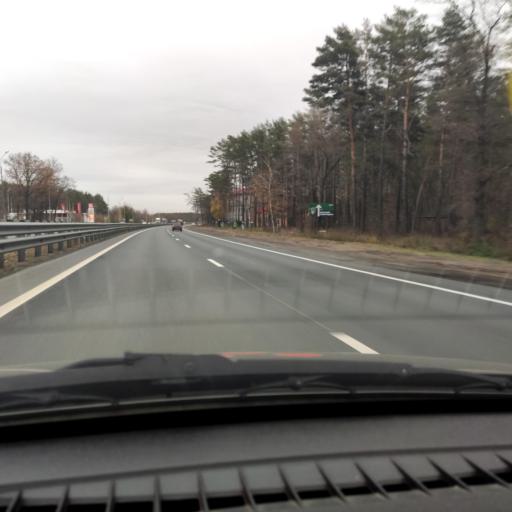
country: RU
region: Samara
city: Zhigulevsk
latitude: 53.5116
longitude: 49.5728
